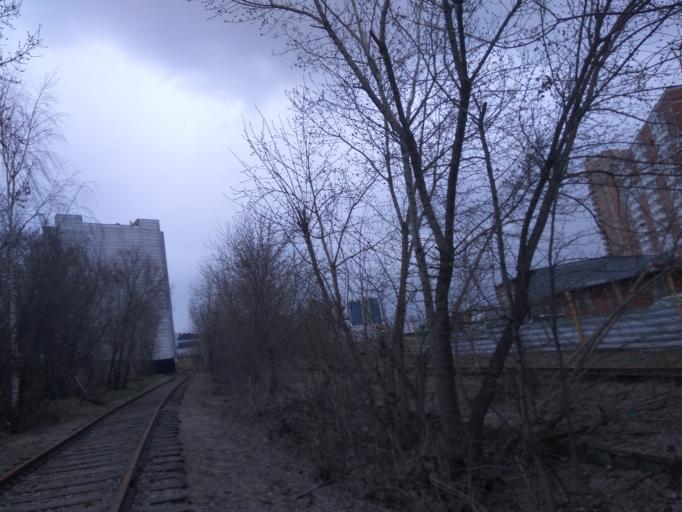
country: RU
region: Moscow
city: Vagonoremont
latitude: 55.9035
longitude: 37.5474
